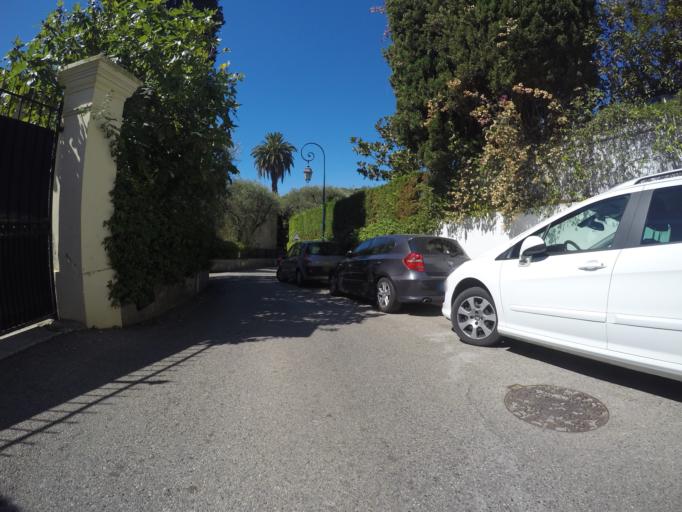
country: FR
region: Provence-Alpes-Cote d'Azur
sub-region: Departement des Alpes-Maritimes
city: Saint-Jean-Cap-Ferrat
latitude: 43.6865
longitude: 7.3384
